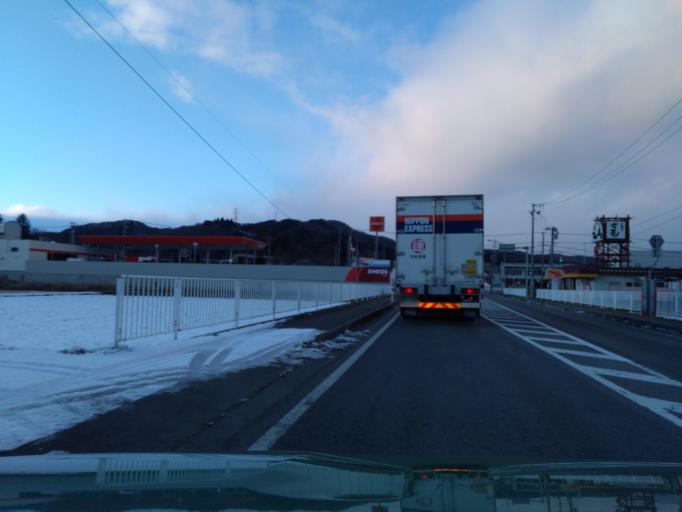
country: JP
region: Iwate
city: Shizukuishi
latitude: 39.6991
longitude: 141.0627
